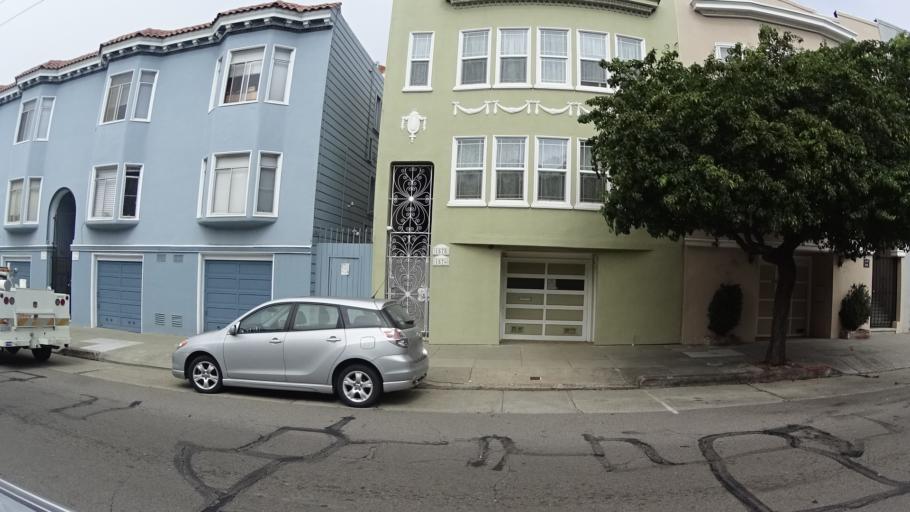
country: US
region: California
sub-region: San Francisco County
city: San Francisco
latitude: 37.8017
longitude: -122.4293
